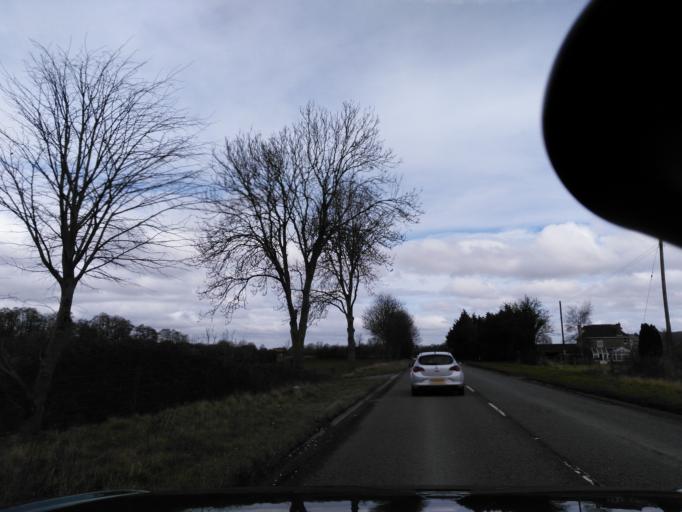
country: GB
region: England
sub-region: Wiltshire
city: Lacock
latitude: 51.4024
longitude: -2.1249
